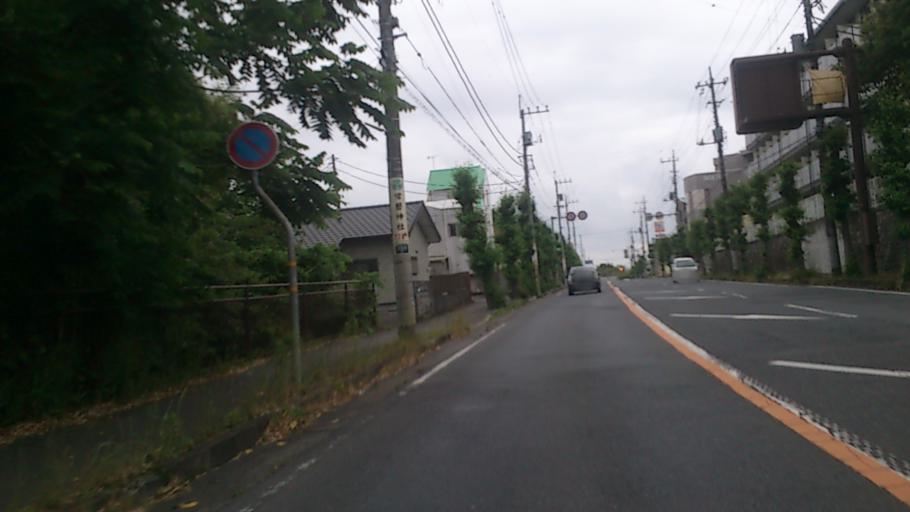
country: JP
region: Ibaraki
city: Mito-shi
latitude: 36.3778
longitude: 140.4588
